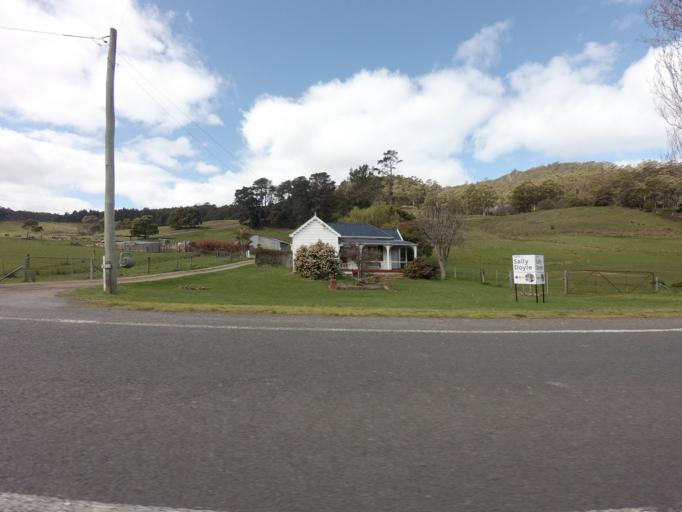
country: AU
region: Tasmania
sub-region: Huon Valley
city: Cygnet
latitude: -43.2953
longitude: 147.0116
